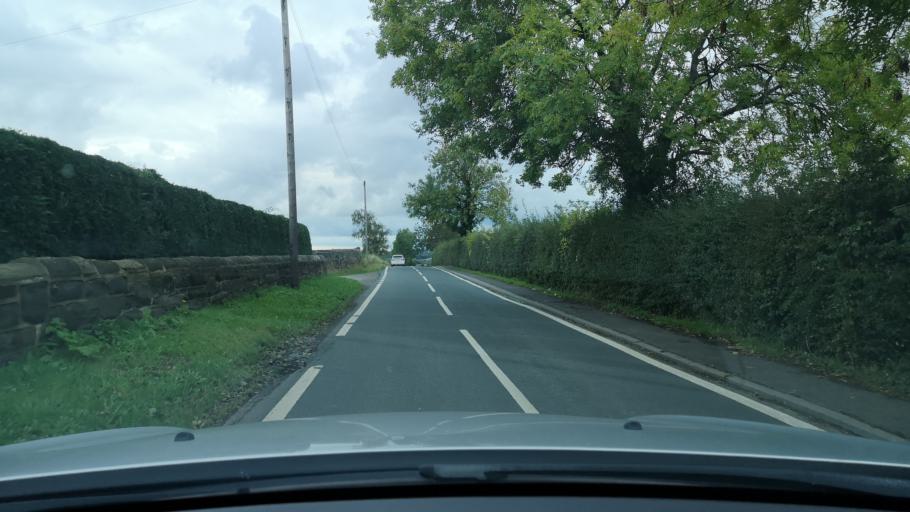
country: GB
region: England
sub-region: City and Borough of Wakefield
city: Low Ackworth
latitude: 53.6565
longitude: -1.3140
